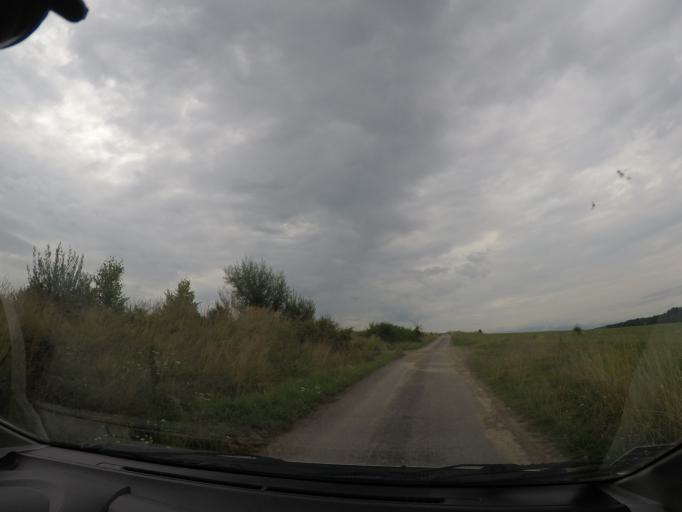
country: SK
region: Nitriansky
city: Bojnice
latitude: 48.9034
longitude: 18.6159
